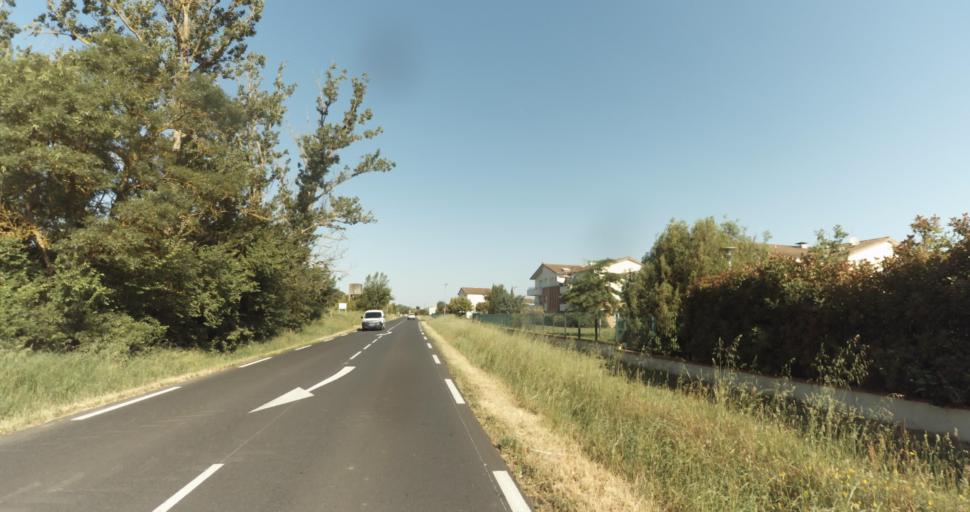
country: FR
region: Midi-Pyrenees
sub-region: Departement de la Haute-Garonne
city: Plaisance-du-Touch
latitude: 43.5519
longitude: 1.3136
